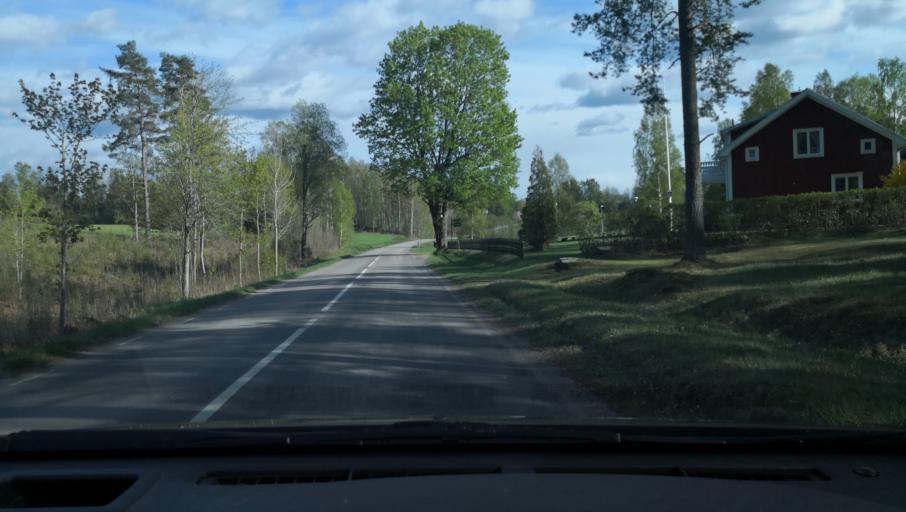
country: SE
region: OErebro
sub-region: Askersunds Kommun
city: Asbro
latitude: 58.9776
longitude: 15.0623
